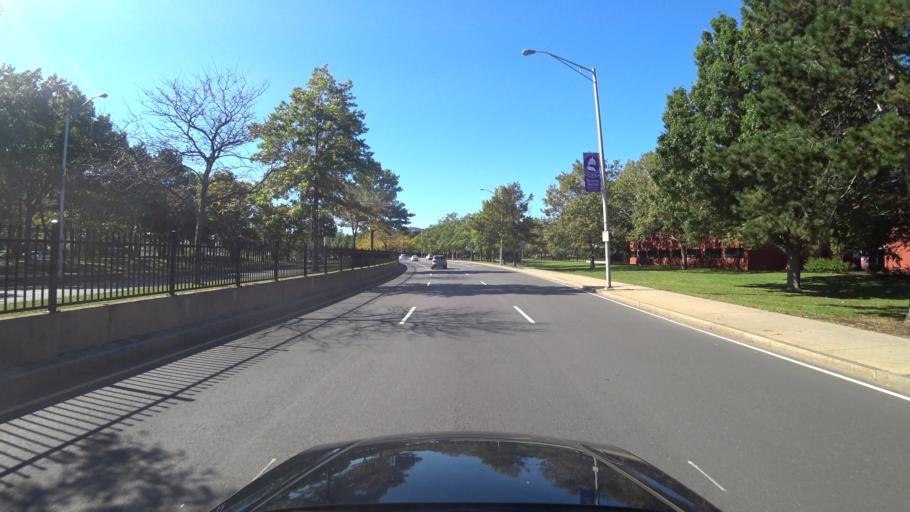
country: US
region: Massachusetts
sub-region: Essex County
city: Lynn
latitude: 42.4599
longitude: -70.9434
